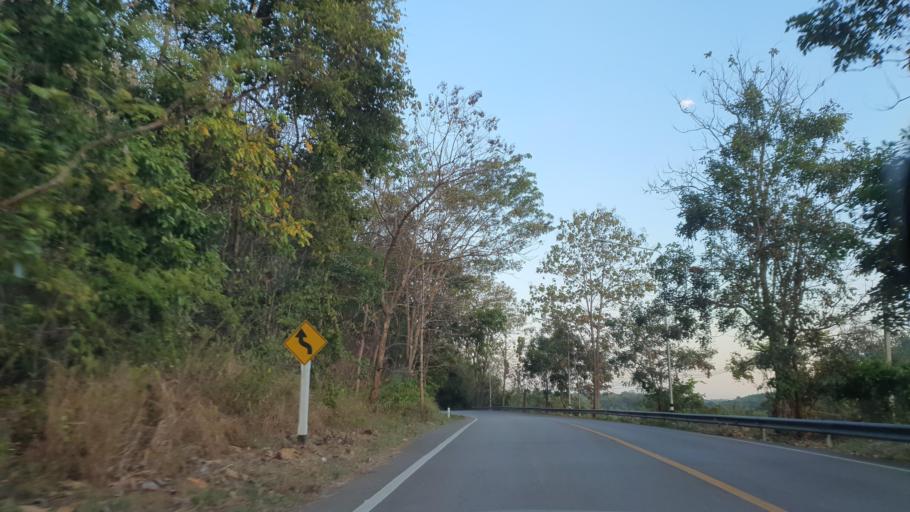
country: TH
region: Chiang Mai
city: Mae Wang
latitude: 18.6174
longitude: 98.7506
